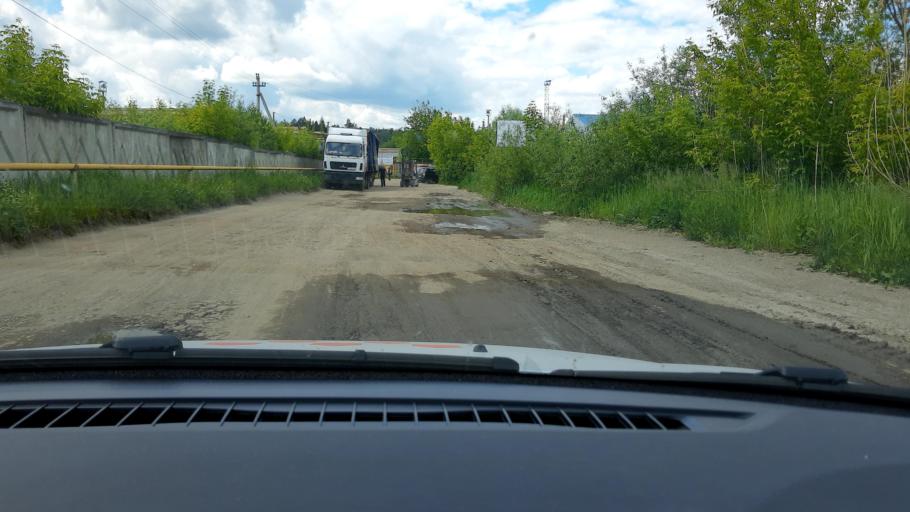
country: RU
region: Nizjnij Novgorod
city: Kstovo
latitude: 56.1714
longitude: 44.1600
